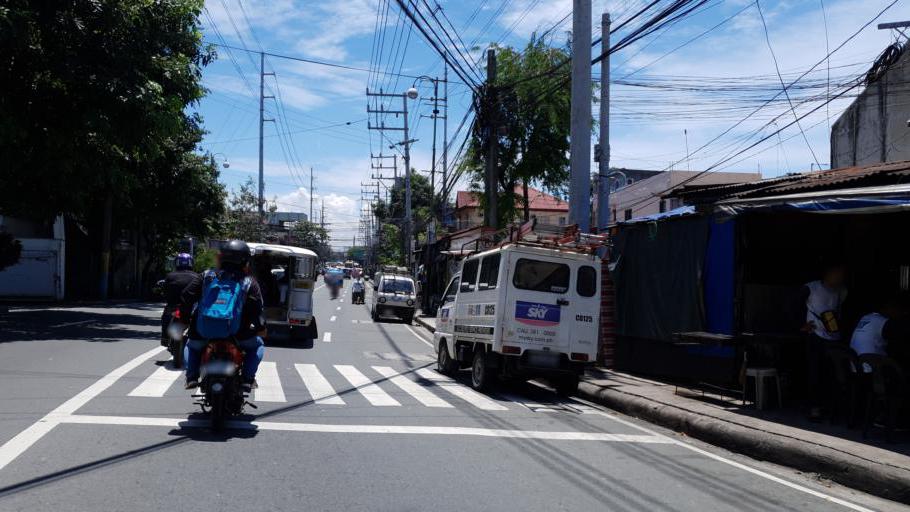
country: PH
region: Calabarzon
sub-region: Province of Rizal
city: Pateros
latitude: 14.5580
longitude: 121.0662
